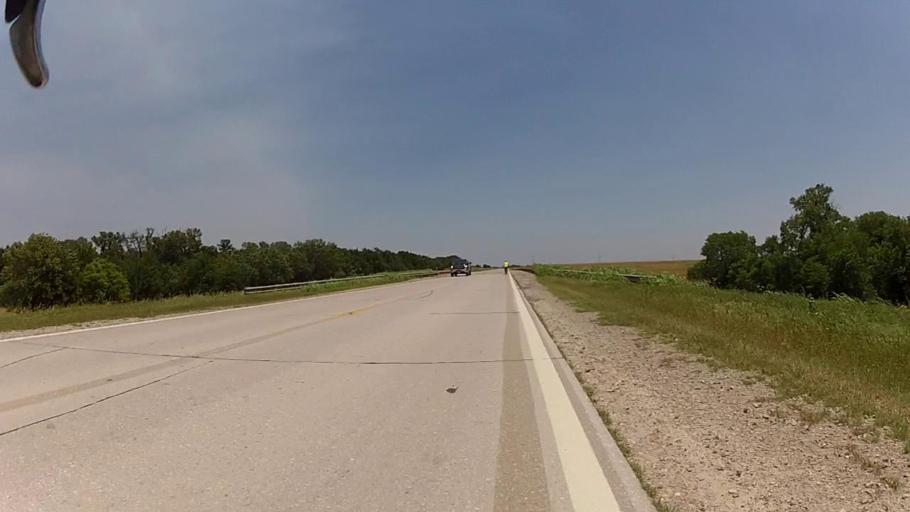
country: US
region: Kansas
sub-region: Sumner County
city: Wellington
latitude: 37.0567
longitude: -97.3882
